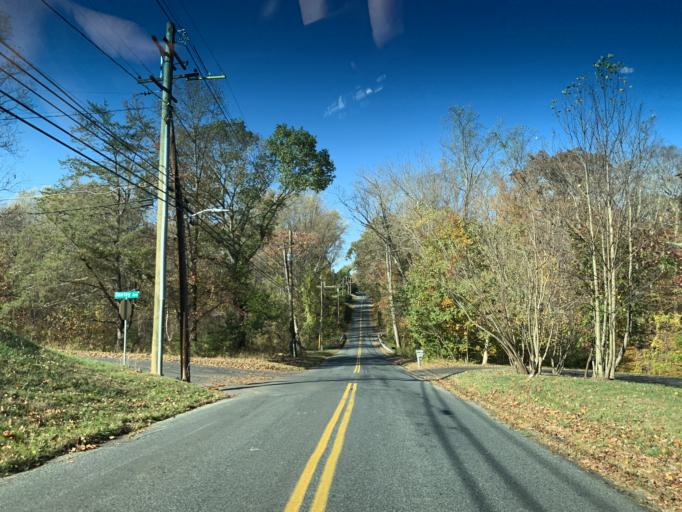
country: US
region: Maryland
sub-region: Harford County
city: Joppatowne
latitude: 39.4567
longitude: -76.3393
